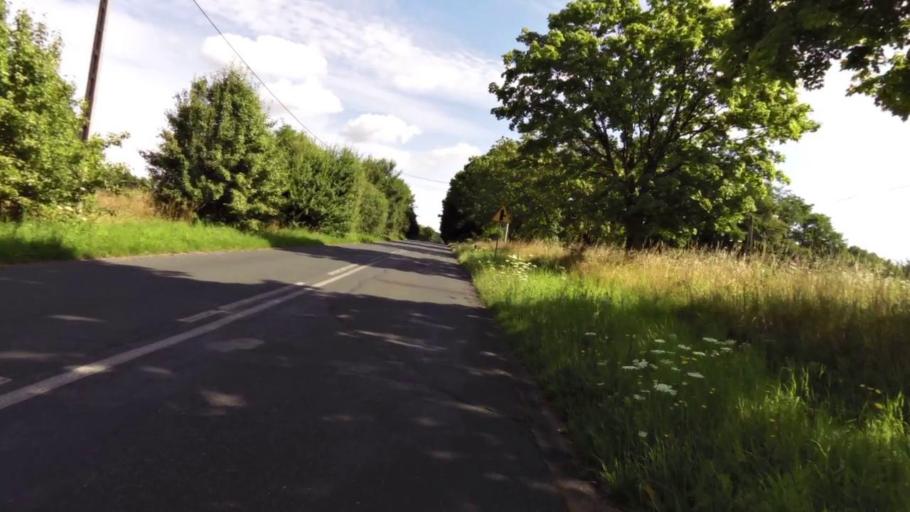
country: PL
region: West Pomeranian Voivodeship
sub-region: Powiat stargardzki
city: Dobrzany
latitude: 53.3718
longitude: 15.4331
